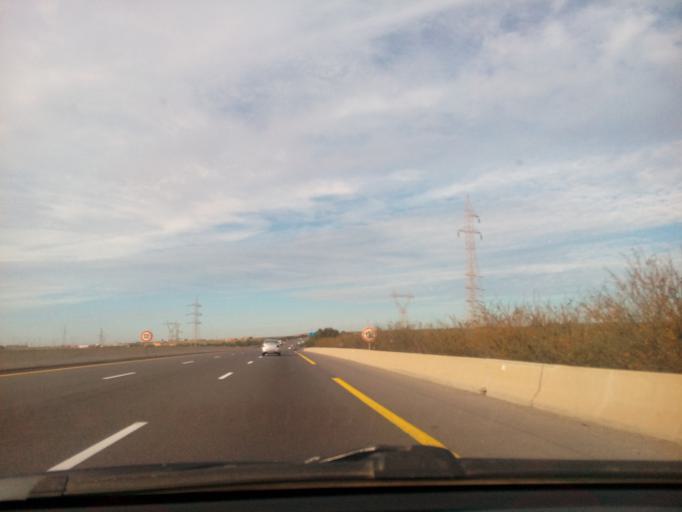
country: DZ
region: Mascara
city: Sig
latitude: 35.5425
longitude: -0.3706
